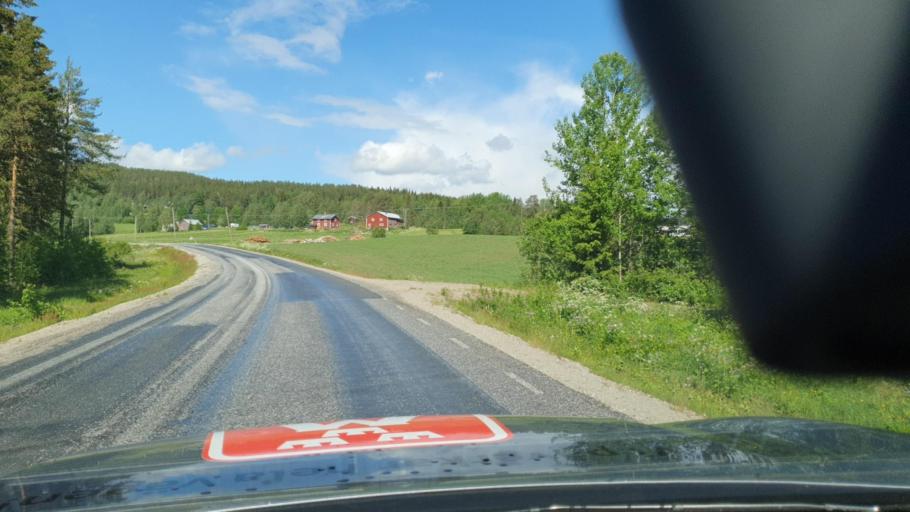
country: SE
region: Vaesternorrland
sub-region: OErnskoeldsviks Kommun
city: Bredbyn
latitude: 63.3629
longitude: 18.0036
